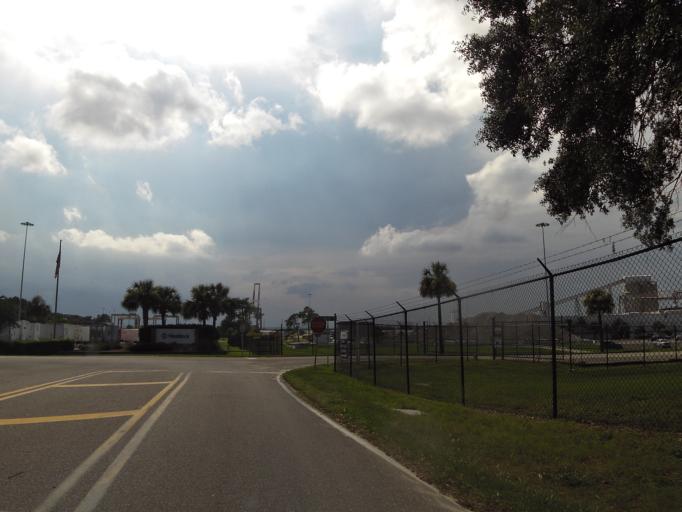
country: US
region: Florida
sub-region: Nassau County
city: Fernandina Beach
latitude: 30.6781
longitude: -81.4557
